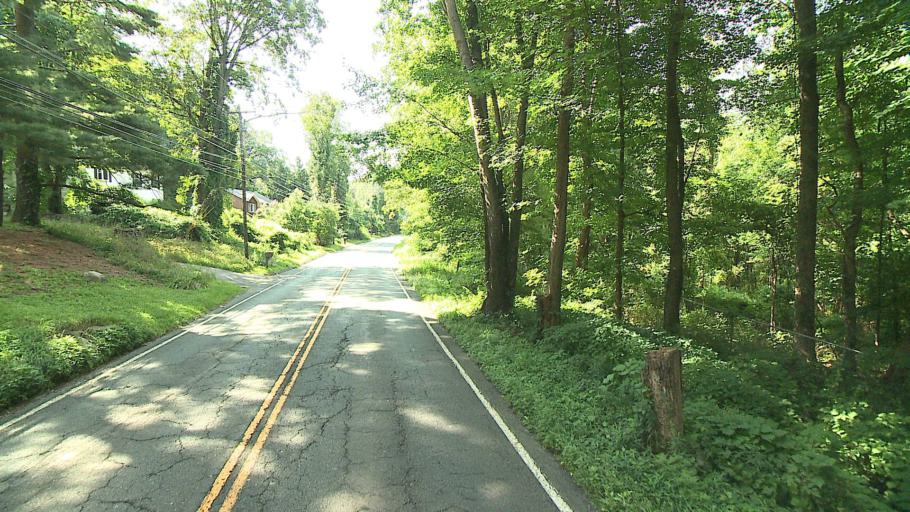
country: US
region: Connecticut
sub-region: Fairfield County
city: Danbury
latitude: 41.4504
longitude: -73.4737
